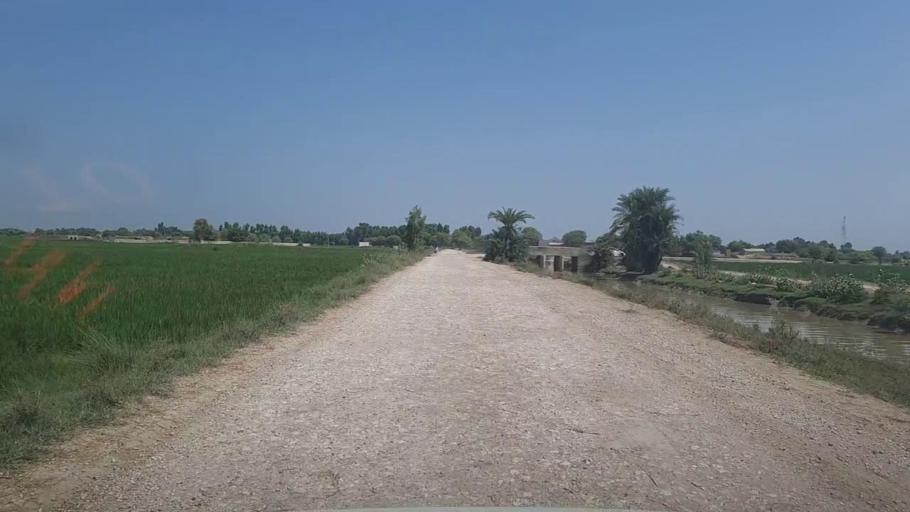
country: PK
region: Sindh
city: Kandhkot
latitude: 28.2708
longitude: 69.2243
